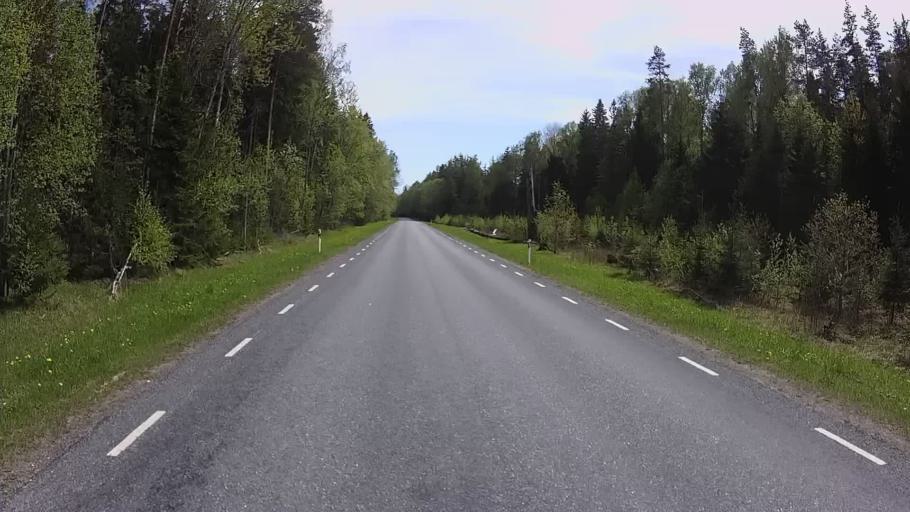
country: EE
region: Valgamaa
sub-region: Valga linn
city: Valga
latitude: 57.6998
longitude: 26.2470
